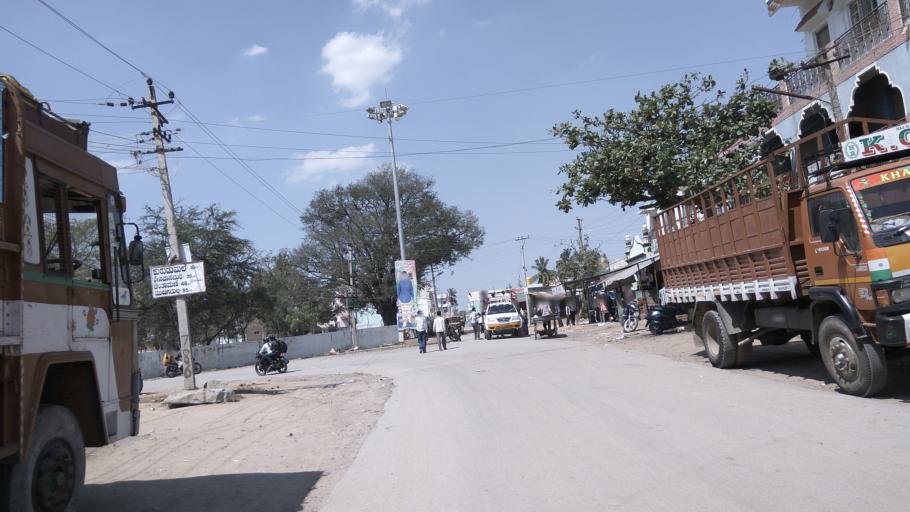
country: IN
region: Karnataka
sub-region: Kolar
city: Mulbagal
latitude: 13.1622
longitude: 78.3851
